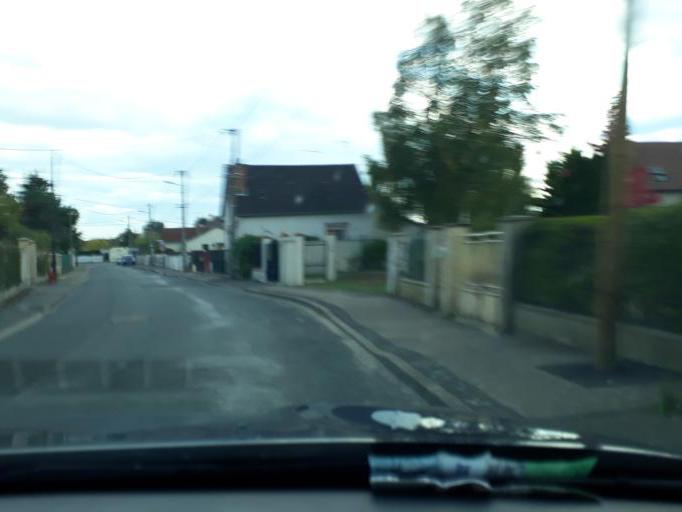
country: FR
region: Centre
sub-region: Departement du Loiret
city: Fleury-les-Aubrais
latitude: 47.9214
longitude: 1.9296
